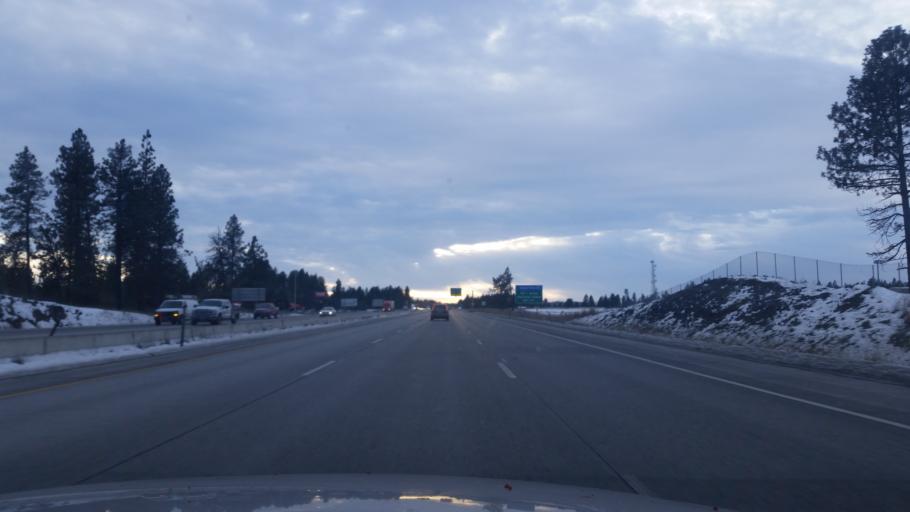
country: US
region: Washington
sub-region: Spokane County
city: Spokane
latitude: 47.6257
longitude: -117.4935
